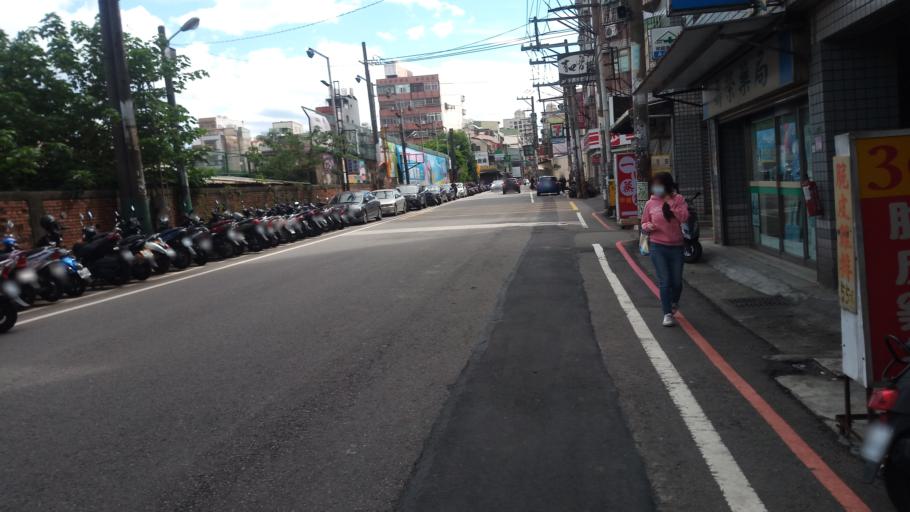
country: TW
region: Taiwan
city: Daxi
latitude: 24.9363
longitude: 121.2495
